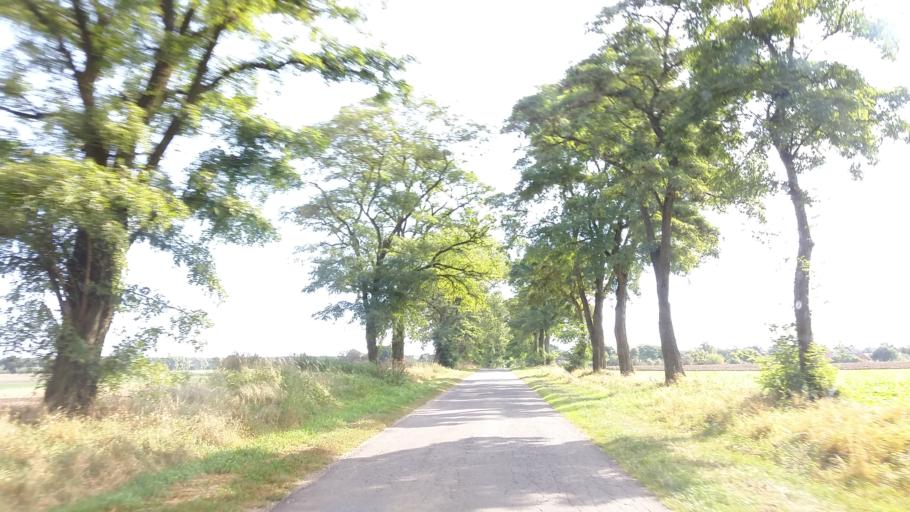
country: PL
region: West Pomeranian Voivodeship
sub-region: Powiat stargardzki
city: Suchan
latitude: 53.2290
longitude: 15.3728
